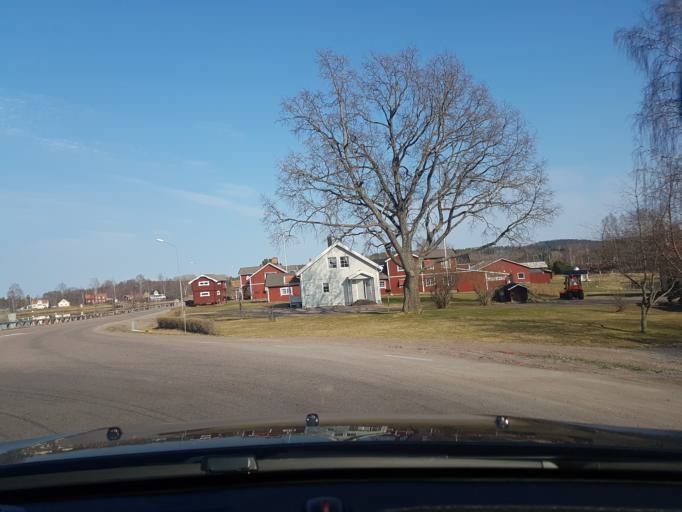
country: SE
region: Dalarna
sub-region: Borlange Kommun
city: Ornas
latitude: 60.4616
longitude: 15.5645
